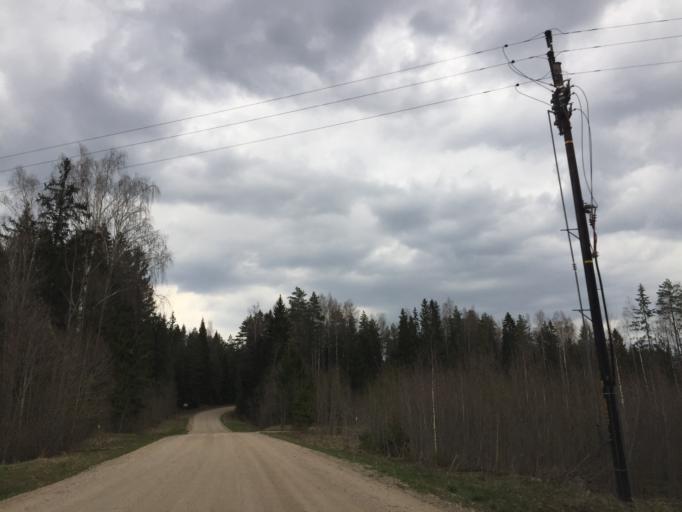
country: EE
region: Vorumaa
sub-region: Antsla vald
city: Vana-Antsla
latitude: 57.9097
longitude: 26.7524
